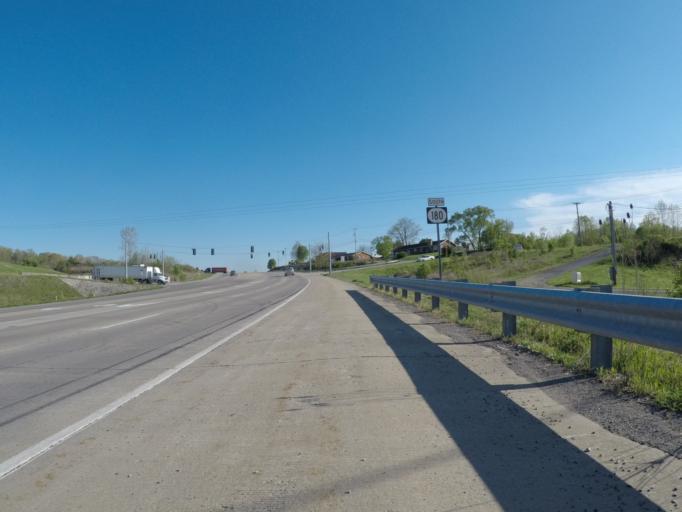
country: US
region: Kentucky
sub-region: Boyd County
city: Meads
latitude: 38.3652
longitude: -82.6990
